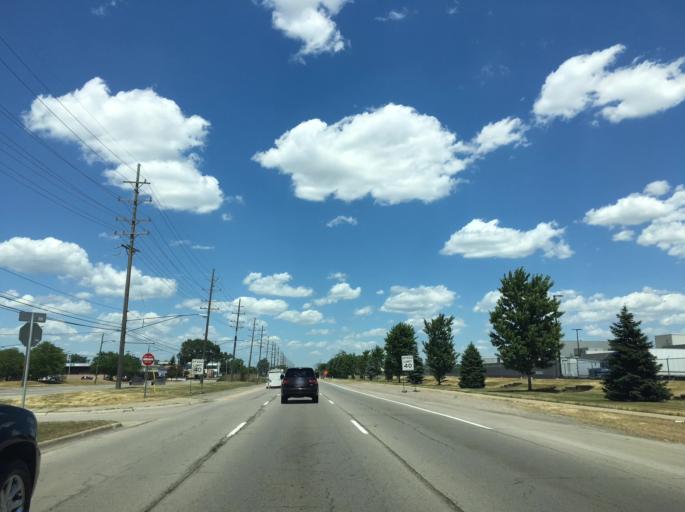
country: US
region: Michigan
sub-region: Macomb County
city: Warren
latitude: 42.4649
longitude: -83.0448
